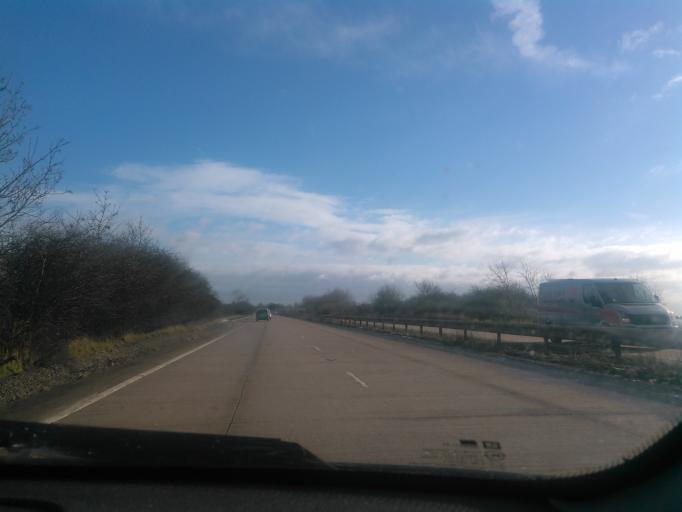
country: GB
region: England
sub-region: Staffordshire
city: Cheadle
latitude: 52.9378
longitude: -1.9857
